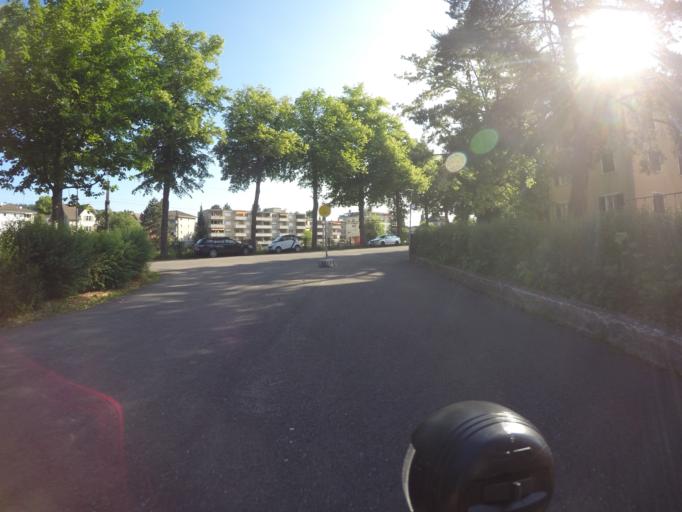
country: CH
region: Zurich
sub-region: Bezirk Winterthur
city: Toess (Kreis 4) / Eichliacker
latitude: 47.4894
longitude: 8.7108
